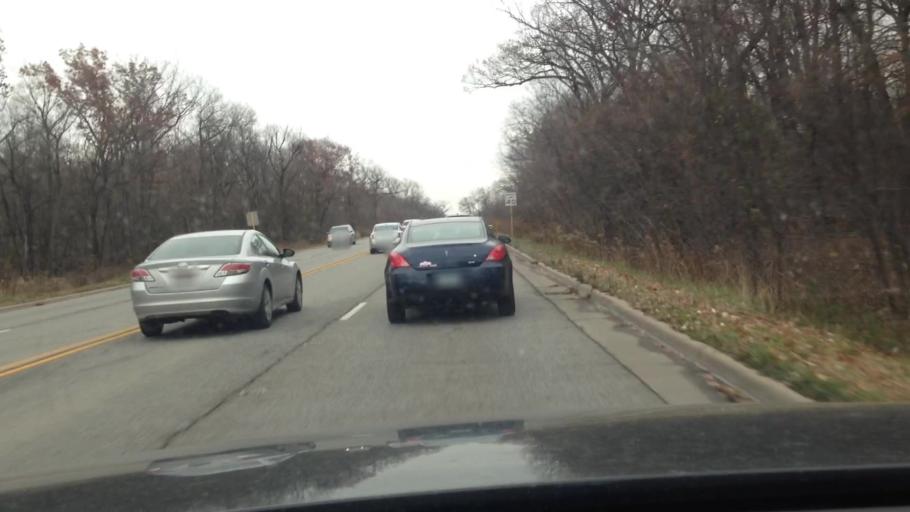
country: US
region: Illinois
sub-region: Cook County
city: River Grove
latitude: 41.9220
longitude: -87.8355
